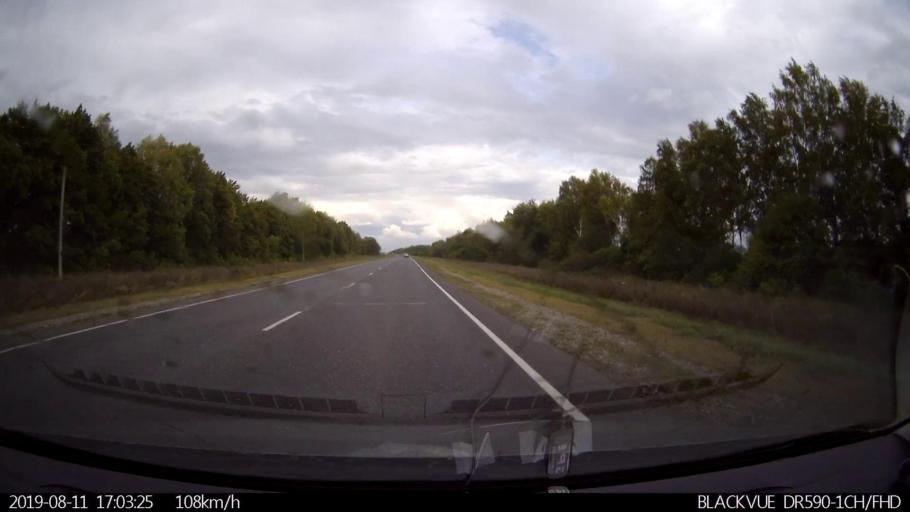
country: RU
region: Ulyanovsk
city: Mayna
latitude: 54.3030
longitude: 47.7398
